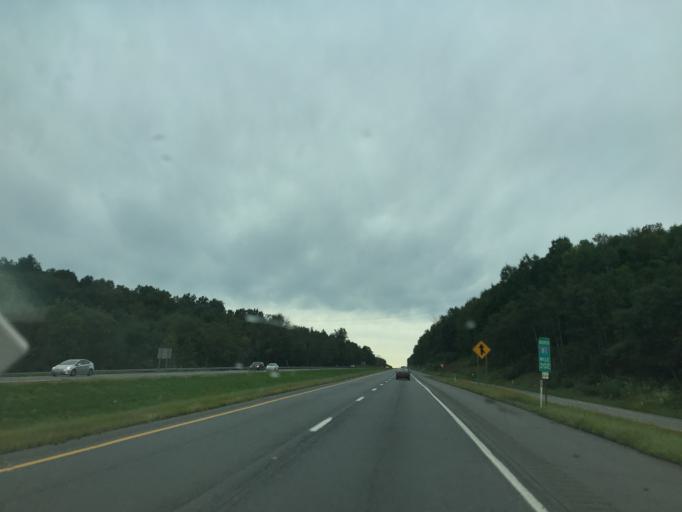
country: US
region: Pennsylvania
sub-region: Lackawanna County
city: Dalton
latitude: 41.5938
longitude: -75.6504
